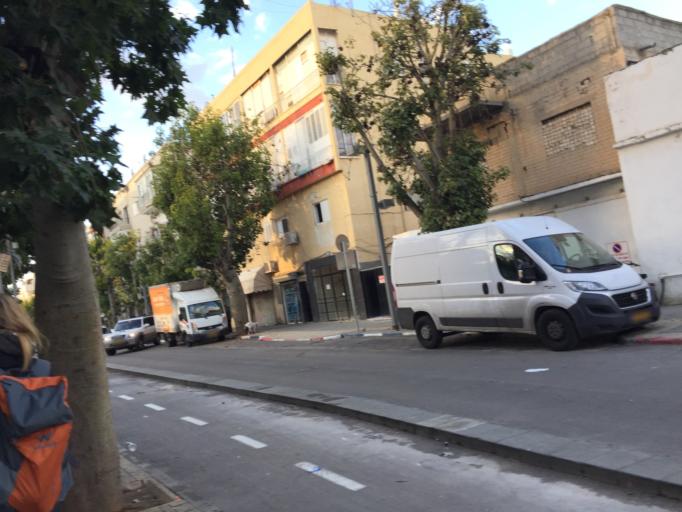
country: IL
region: Tel Aviv
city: Tel Aviv
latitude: 32.0573
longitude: 34.7763
